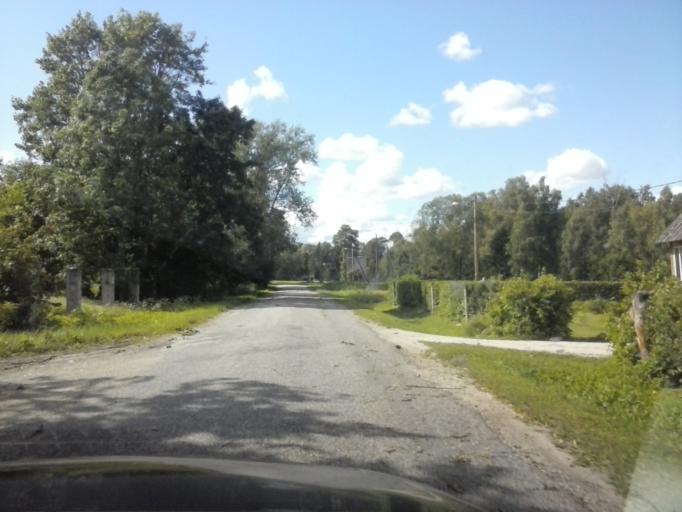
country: EE
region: Laeaene-Virumaa
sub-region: Vaeike-Maarja vald
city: Vaike-Maarja
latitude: 59.0854
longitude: 26.1831
